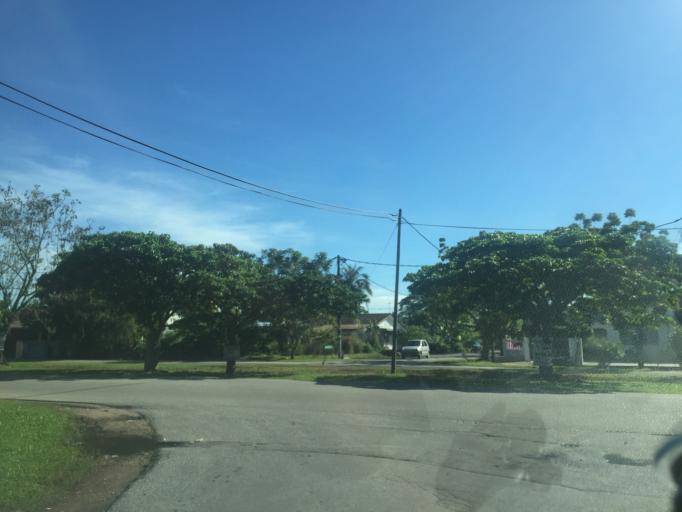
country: MY
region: Penang
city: Tasek Glugor
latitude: 5.5141
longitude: 100.5457
